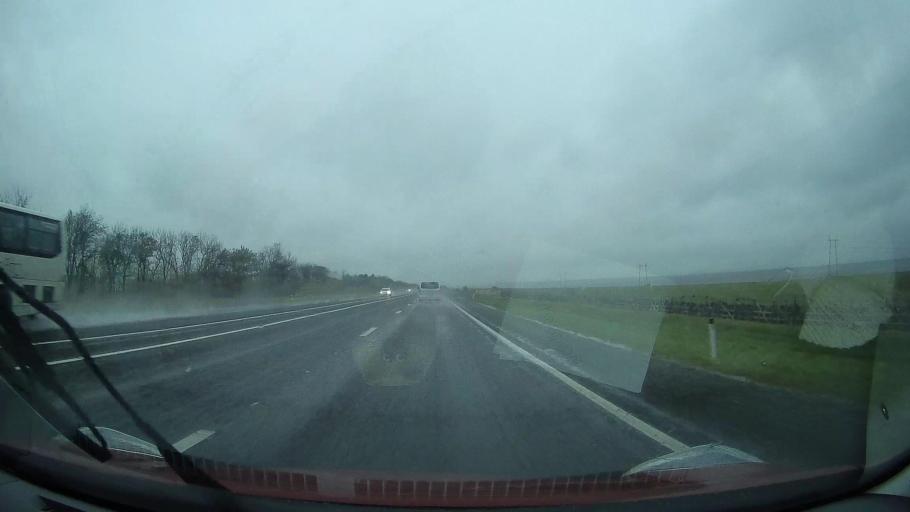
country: RU
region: Stavropol'skiy
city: Nevinnomyssk
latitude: 44.6118
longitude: 42.1195
